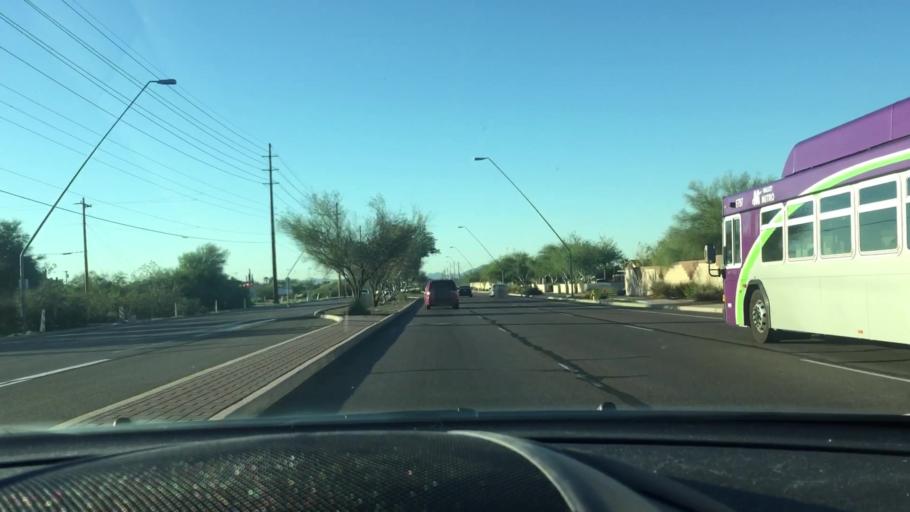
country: US
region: Arizona
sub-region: Pinal County
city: Apache Junction
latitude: 33.4430
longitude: -111.6843
